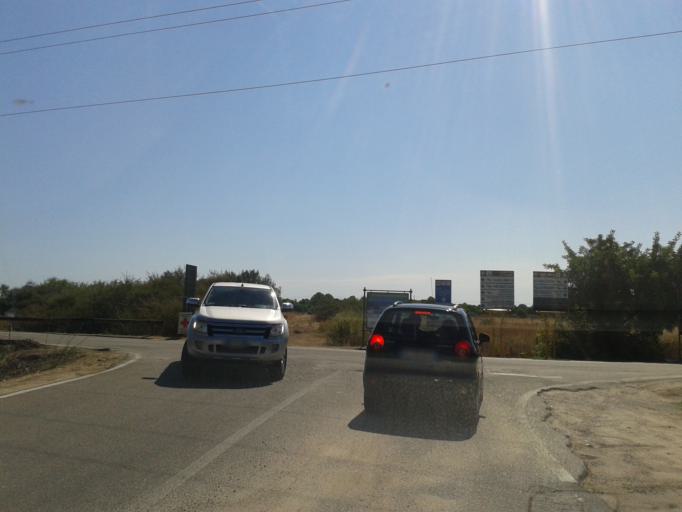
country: IT
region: Sardinia
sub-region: Provincia di Cagliari
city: Olia Speciosa
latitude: 39.2398
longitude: 9.5603
